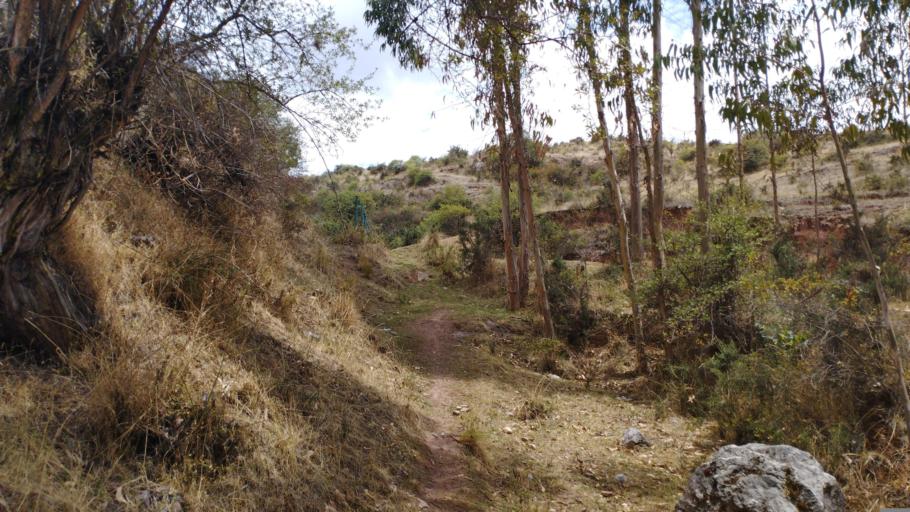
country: PE
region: Cusco
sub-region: Provincia de Cusco
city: Cusco
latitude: -13.5173
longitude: -71.9432
